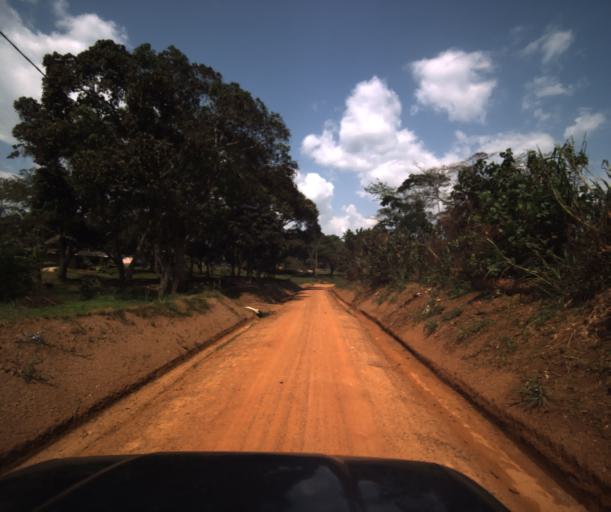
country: CM
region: Centre
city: Akono
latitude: 3.5450
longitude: 11.0446
